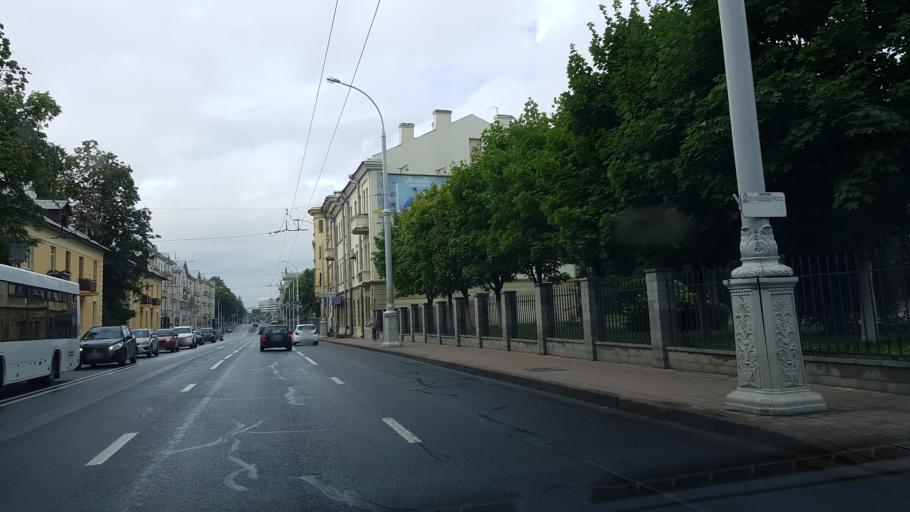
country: BY
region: Minsk
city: Minsk
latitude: 53.9145
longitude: 27.5620
